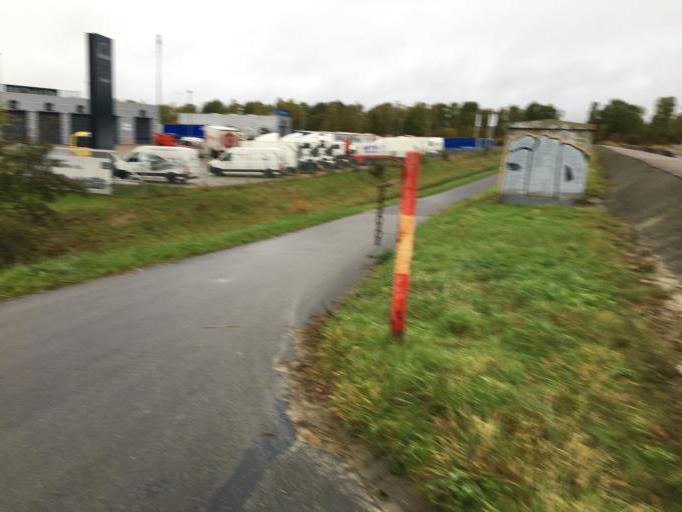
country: DK
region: Capital Region
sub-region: Hvidovre Kommune
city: Hvidovre
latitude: 55.6128
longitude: 12.4969
